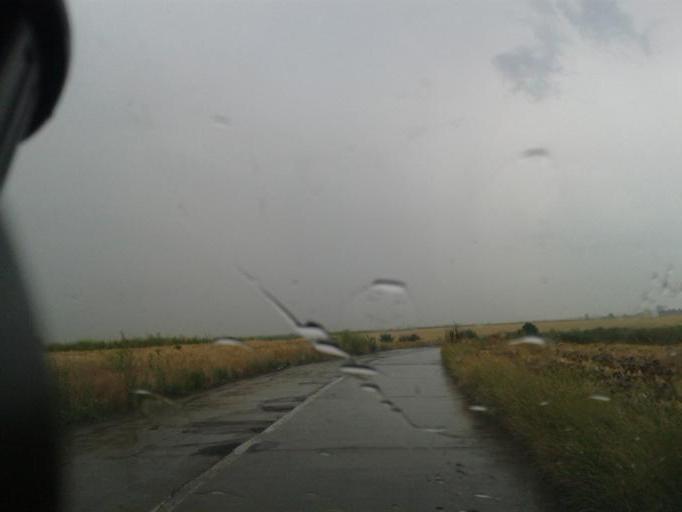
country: RO
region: Ialomita
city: Sinesti
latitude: 44.5398
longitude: 26.3902
